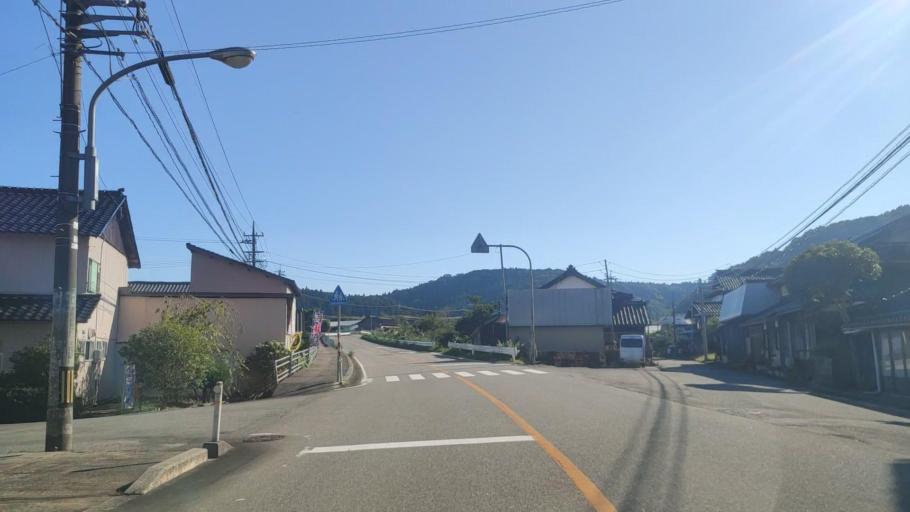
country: JP
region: Ishikawa
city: Nanao
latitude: 37.1451
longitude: 136.8722
